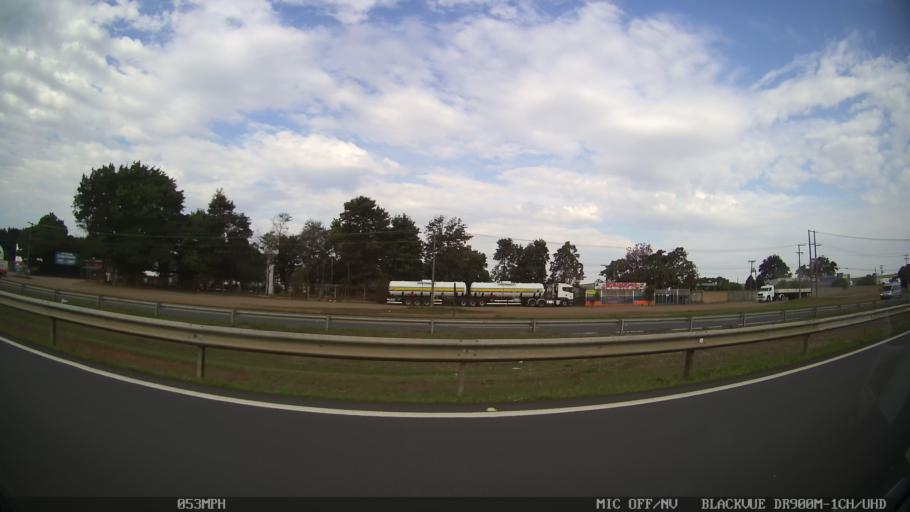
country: BR
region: Sao Paulo
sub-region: Paulinia
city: Paulinia
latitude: -22.7350
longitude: -47.1541
